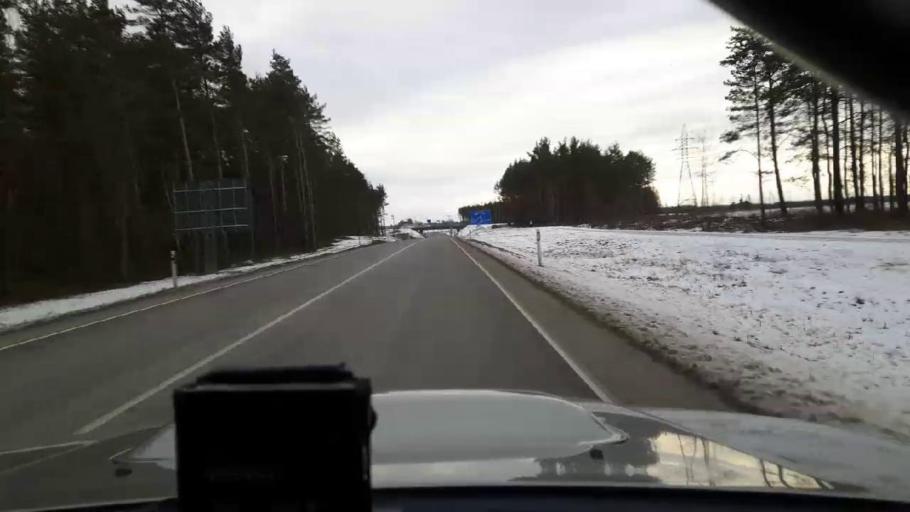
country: EE
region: Harju
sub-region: Saue vald
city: Laagri
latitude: 59.3444
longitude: 24.6028
